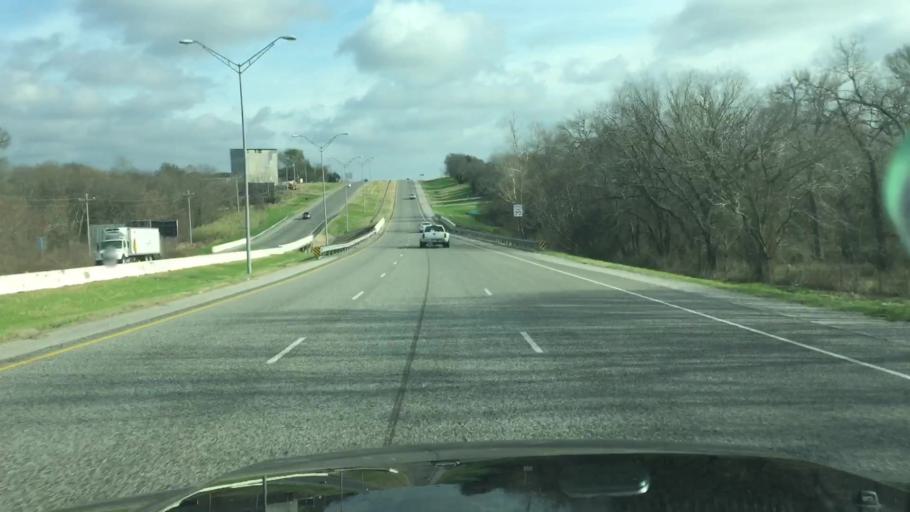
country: US
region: Texas
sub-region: Washington County
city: Brenham
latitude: 30.1416
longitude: -96.3601
